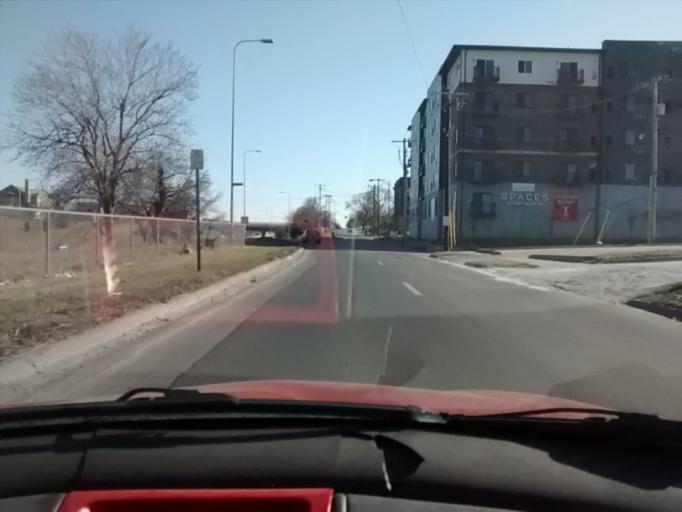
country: US
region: Nebraska
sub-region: Douglas County
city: Omaha
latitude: 41.2565
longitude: -95.9545
